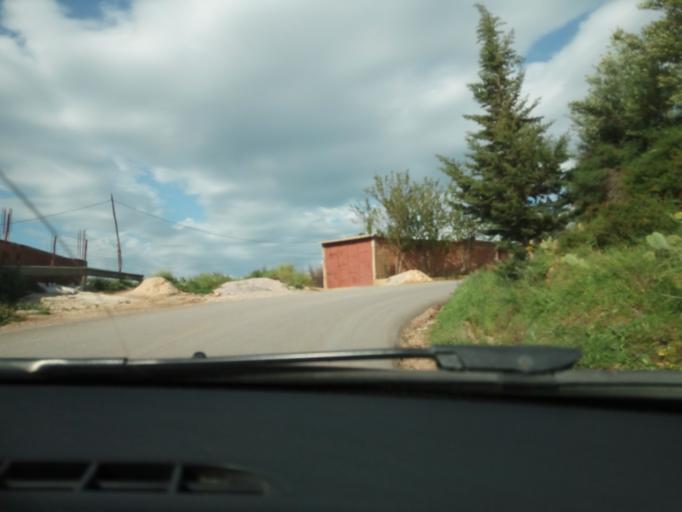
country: DZ
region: Tipaza
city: Hadjout
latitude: 36.3741
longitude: 2.4809
